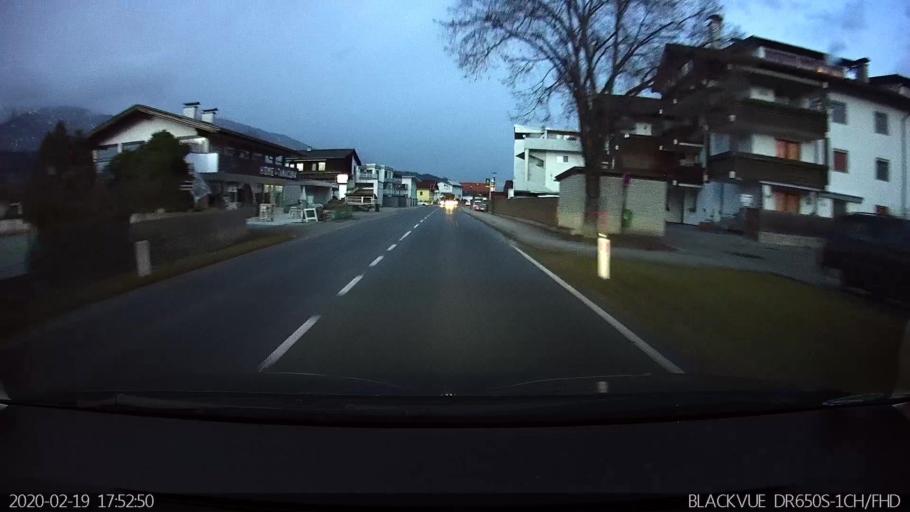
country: AT
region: Tyrol
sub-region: Politischer Bezirk Innsbruck Land
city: Volders
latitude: 47.2857
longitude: 11.5611
